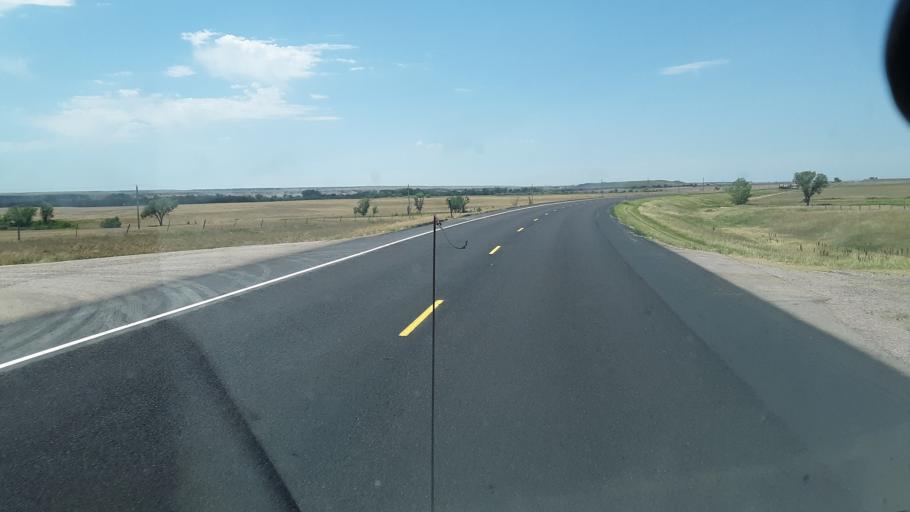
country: US
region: South Dakota
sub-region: Haakon County
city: Philip
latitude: 43.7096
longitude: -102.0478
